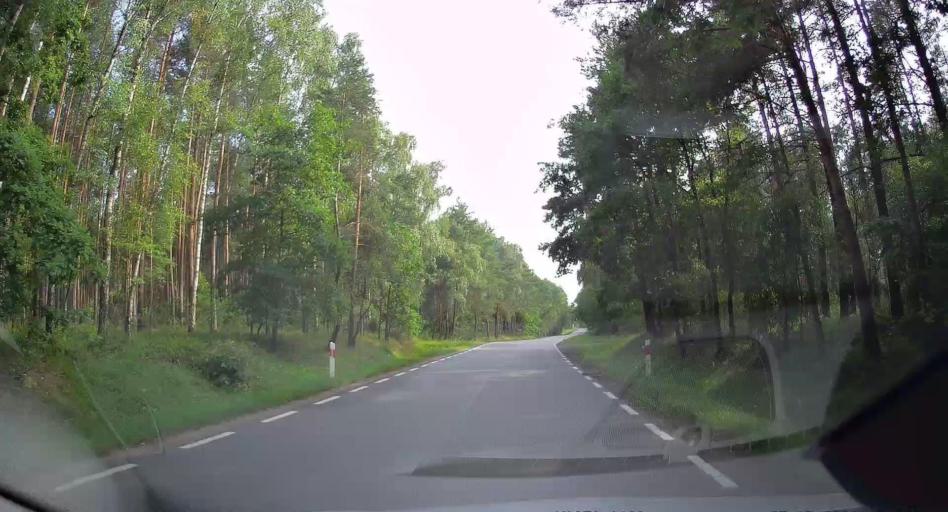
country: PL
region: Lodz Voivodeship
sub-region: Powiat tomaszowski
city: Inowlodz
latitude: 51.5404
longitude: 20.2343
